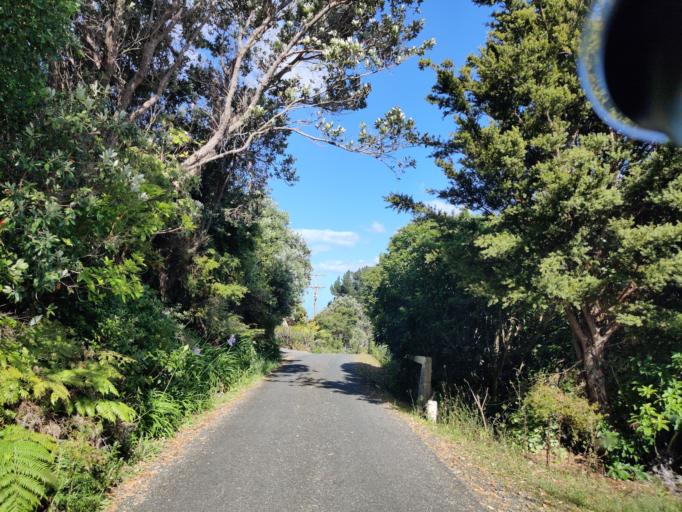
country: NZ
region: Northland
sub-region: Whangarei
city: Ngunguru
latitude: -35.6109
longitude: 174.5323
